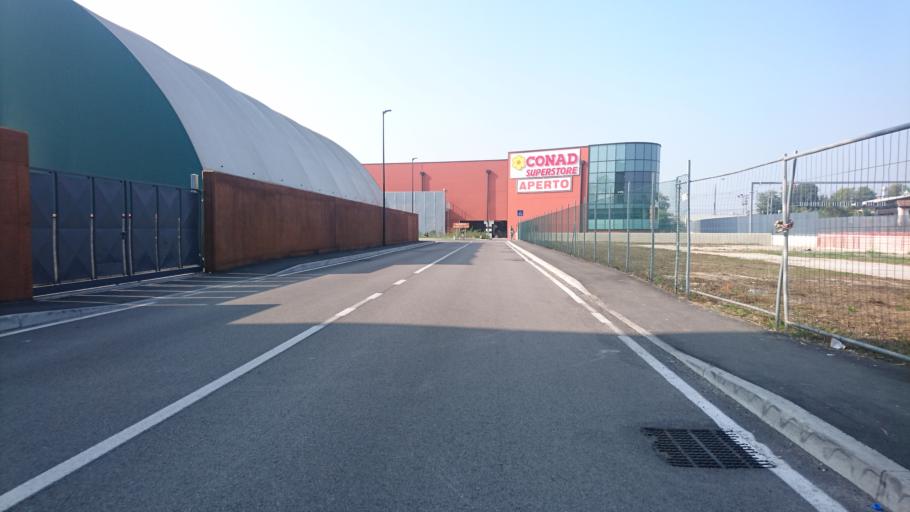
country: IT
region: Veneto
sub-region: Provincia di Padova
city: Padova
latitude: 45.4175
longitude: 11.8629
